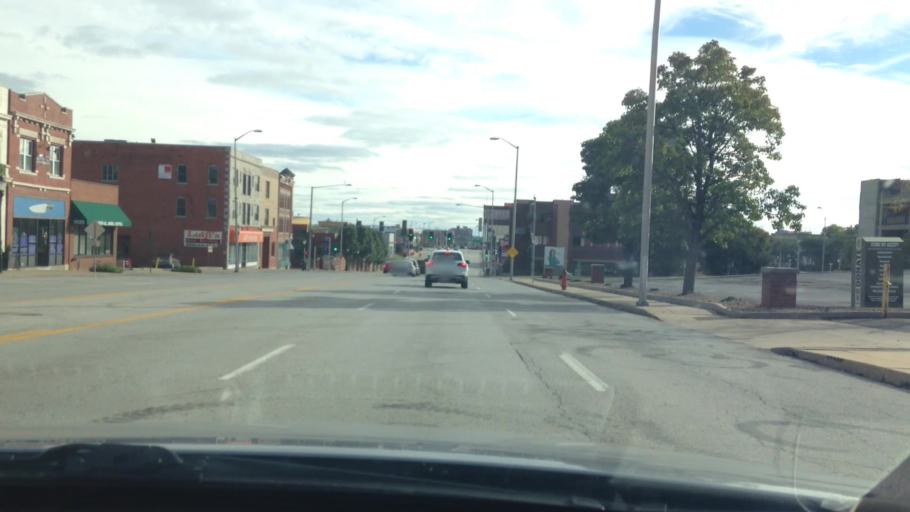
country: US
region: Missouri
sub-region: Jackson County
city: Kansas City
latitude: 39.0723
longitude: -94.5853
